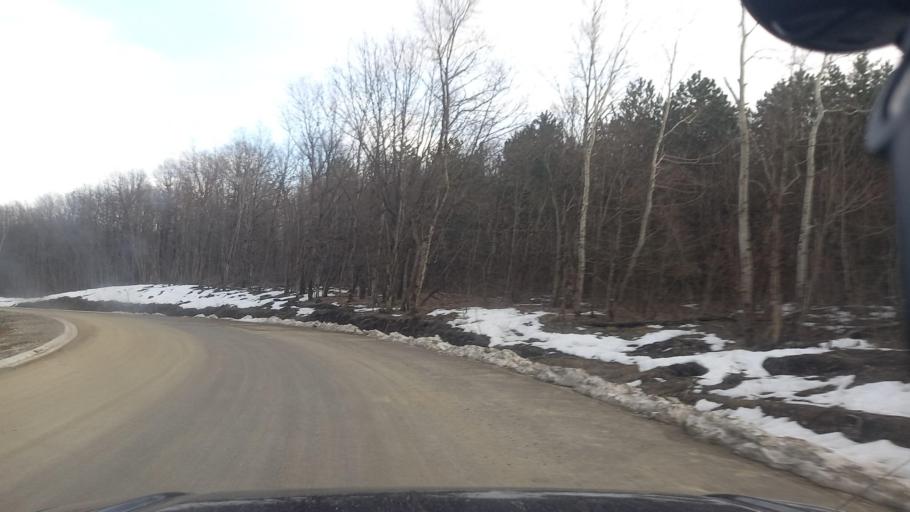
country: RU
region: Krasnodarskiy
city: Goryachiy Klyuch
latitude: 44.6980
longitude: 38.9865
